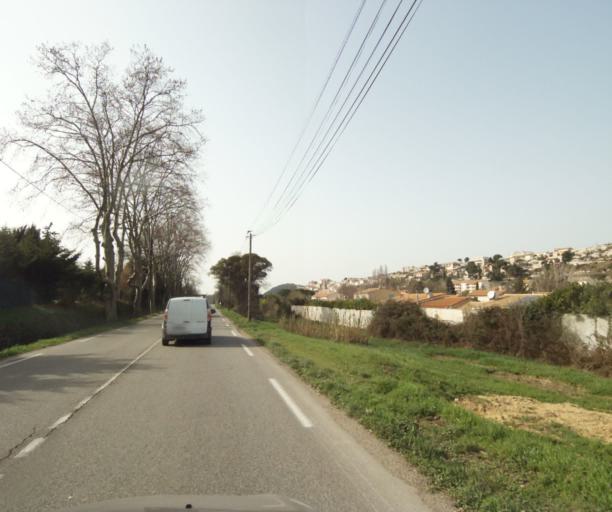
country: FR
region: Provence-Alpes-Cote d'Azur
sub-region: Departement des Bouches-du-Rhone
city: Les Pennes-Mirabeau
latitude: 43.4085
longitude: 5.3177
